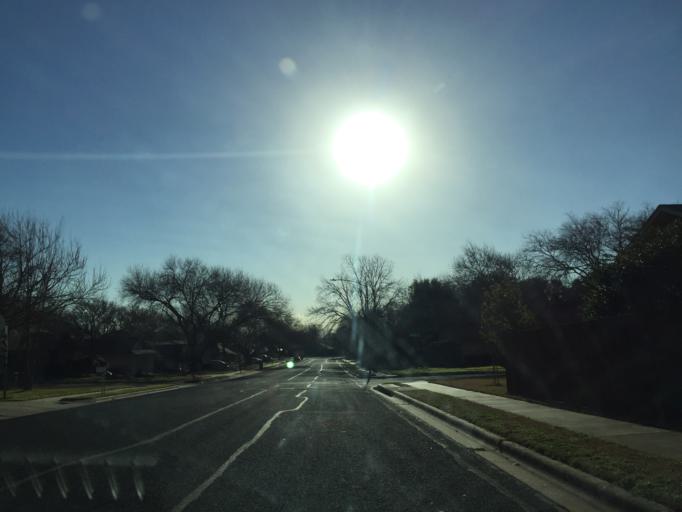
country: US
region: Texas
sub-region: Williamson County
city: Jollyville
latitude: 30.4108
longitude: -97.7388
